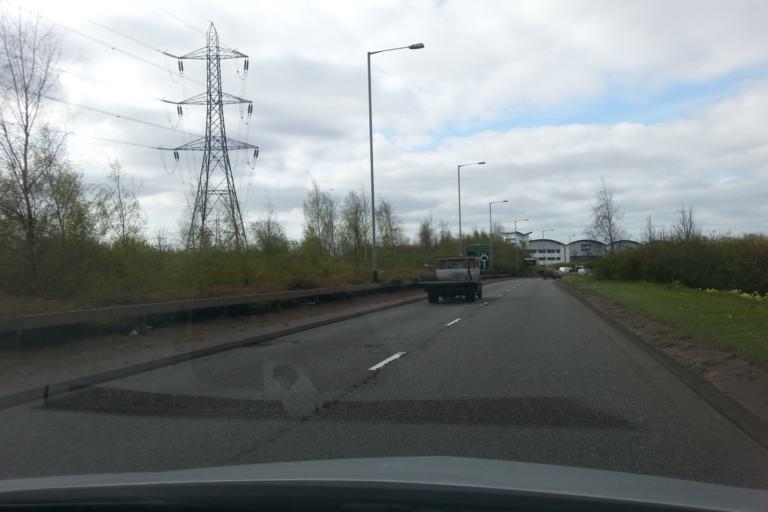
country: GB
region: England
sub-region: Wolverhampton
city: Bilston
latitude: 52.5712
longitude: -2.0521
